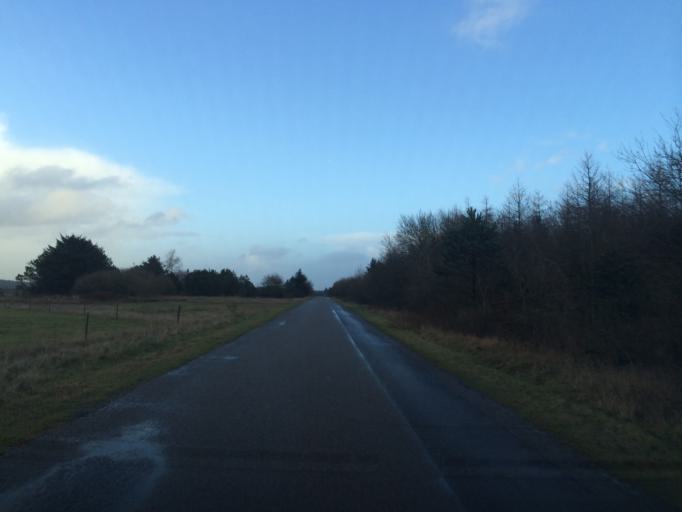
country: DK
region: Central Jutland
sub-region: Holstebro Kommune
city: Ulfborg
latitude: 56.2410
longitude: 8.3967
